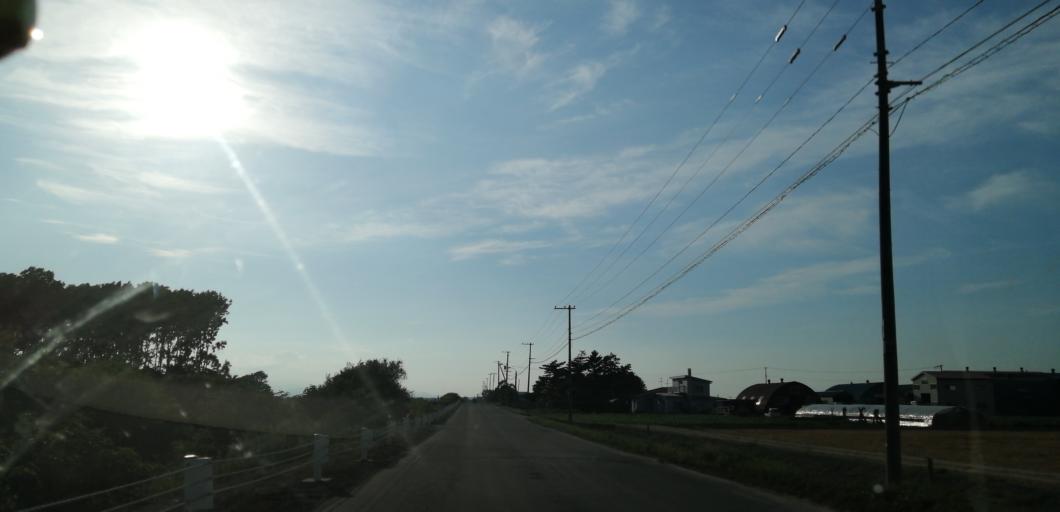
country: JP
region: Hokkaido
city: Kitahiroshima
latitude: 42.9548
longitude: 141.6578
